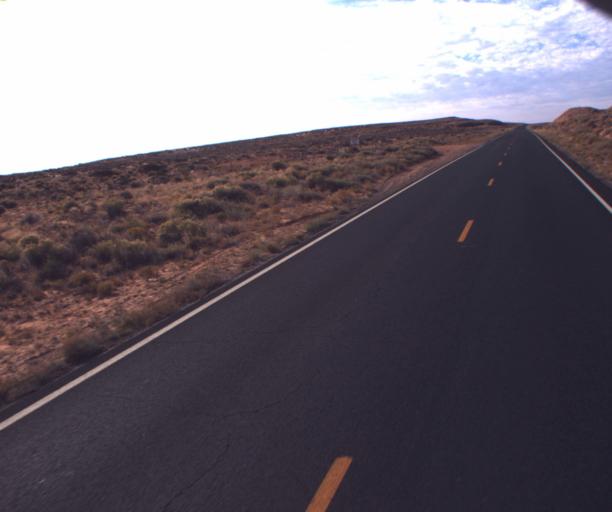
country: US
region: Arizona
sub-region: Apache County
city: Many Farms
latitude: 36.8907
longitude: -109.6270
